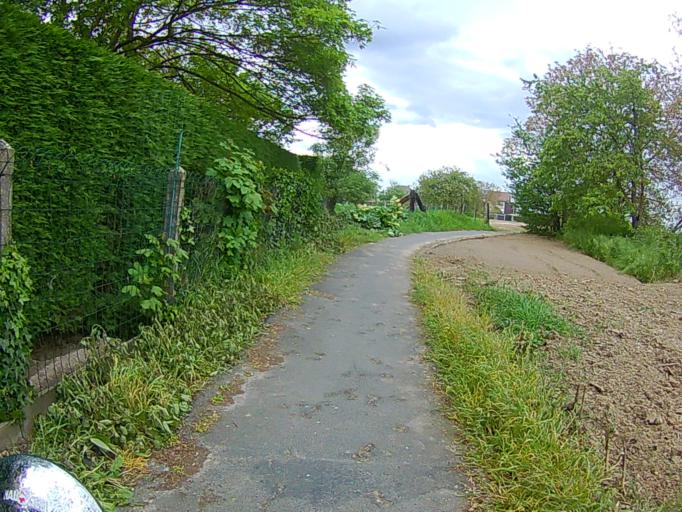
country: BE
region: Flanders
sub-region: Provincie Vlaams-Brabant
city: Opwijk
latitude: 50.9551
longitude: 4.1770
